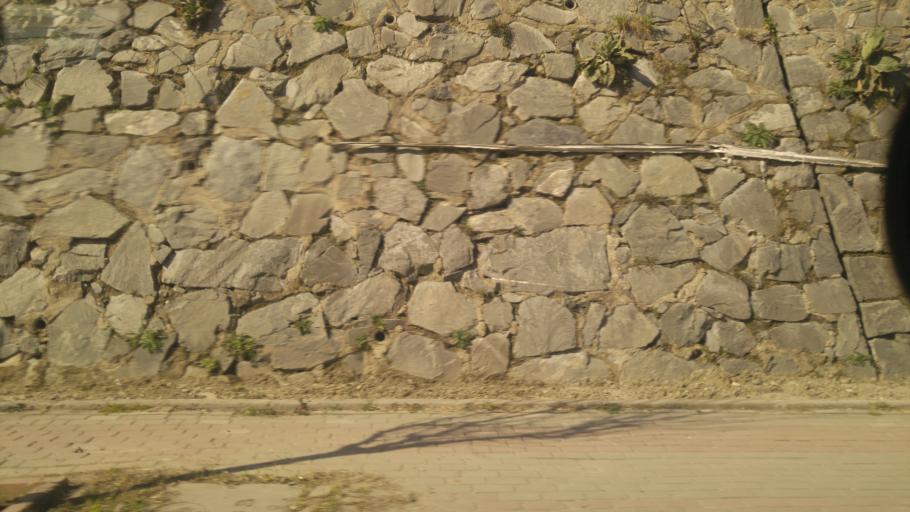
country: TR
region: Istanbul
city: Basaksehir
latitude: 41.0913
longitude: 28.8024
